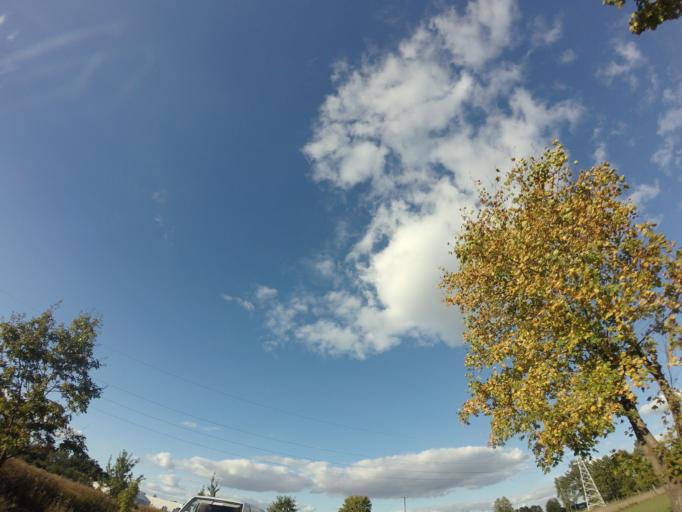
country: PL
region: Greater Poland Voivodeship
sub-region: Powiat nowotomyski
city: Nowy Tomysl
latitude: 52.2933
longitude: 16.1268
